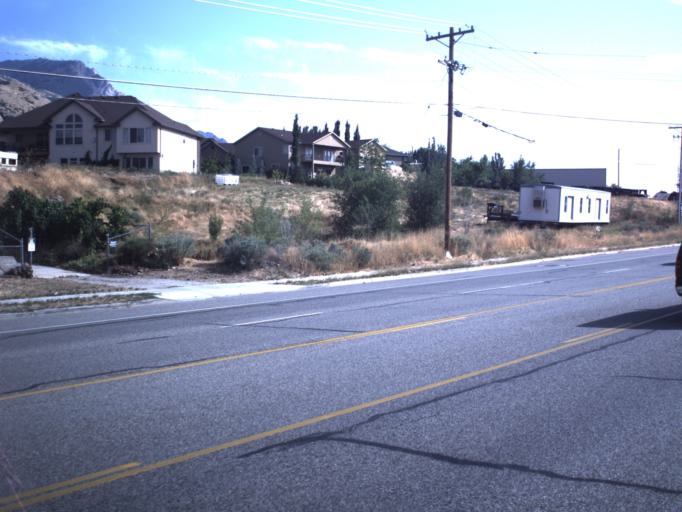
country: US
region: Utah
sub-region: Box Elder County
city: Perry
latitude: 41.4619
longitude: -112.0362
